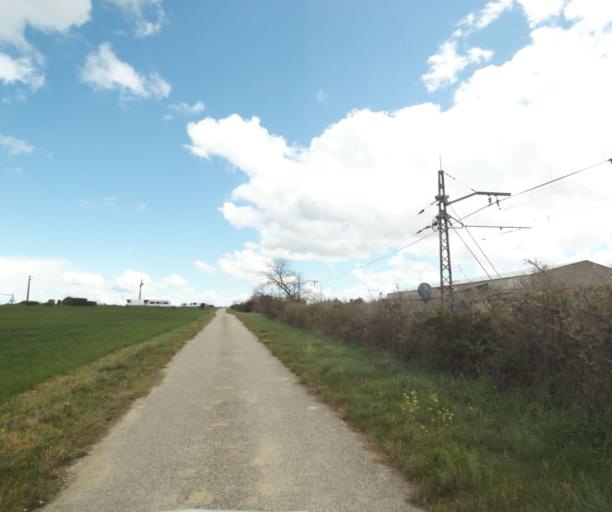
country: FR
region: Midi-Pyrenees
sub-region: Departement de l'Ariege
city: Saverdun
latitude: 43.2335
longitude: 1.5938
